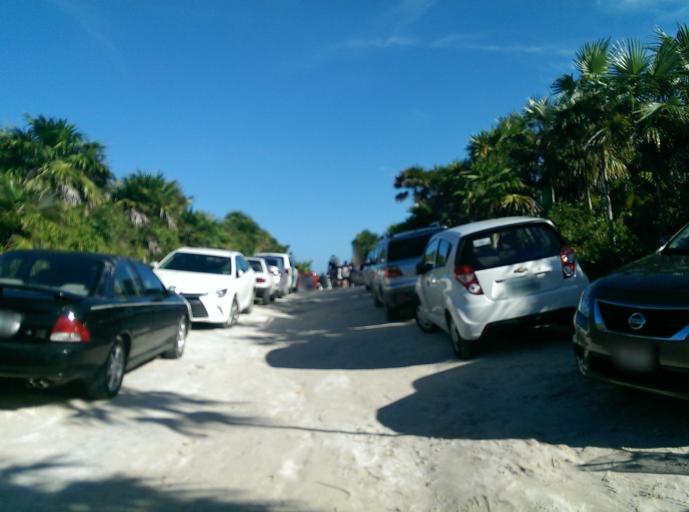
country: MX
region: Quintana Roo
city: Tulum
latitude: 20.2033
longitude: -87.4339
